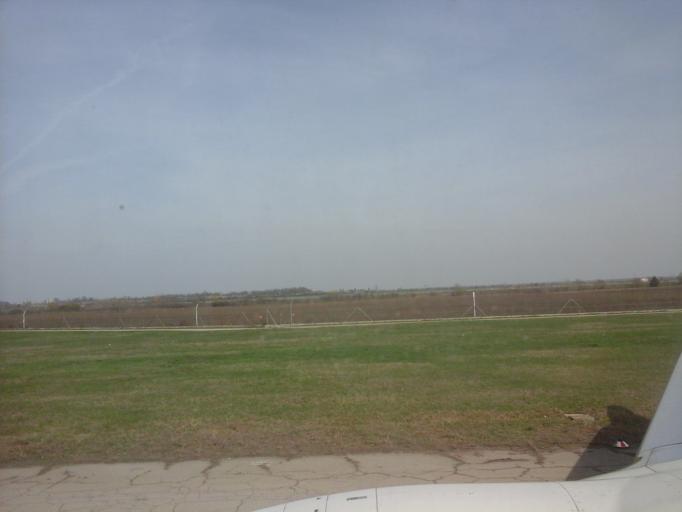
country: RO
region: Ilfov
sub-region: Comuna Otopeni
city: Otopeni
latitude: 44.5705
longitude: 26.1028
